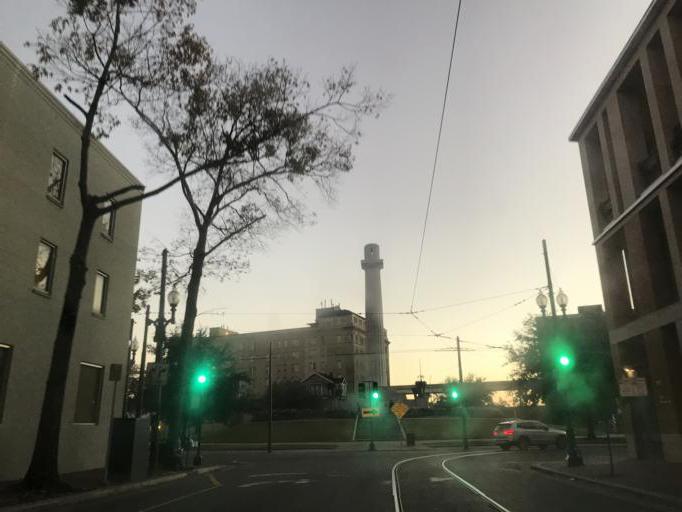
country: US
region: Louisiana
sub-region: Orleans Parish
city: New Orleans
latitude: 29.9441
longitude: -90.0722
